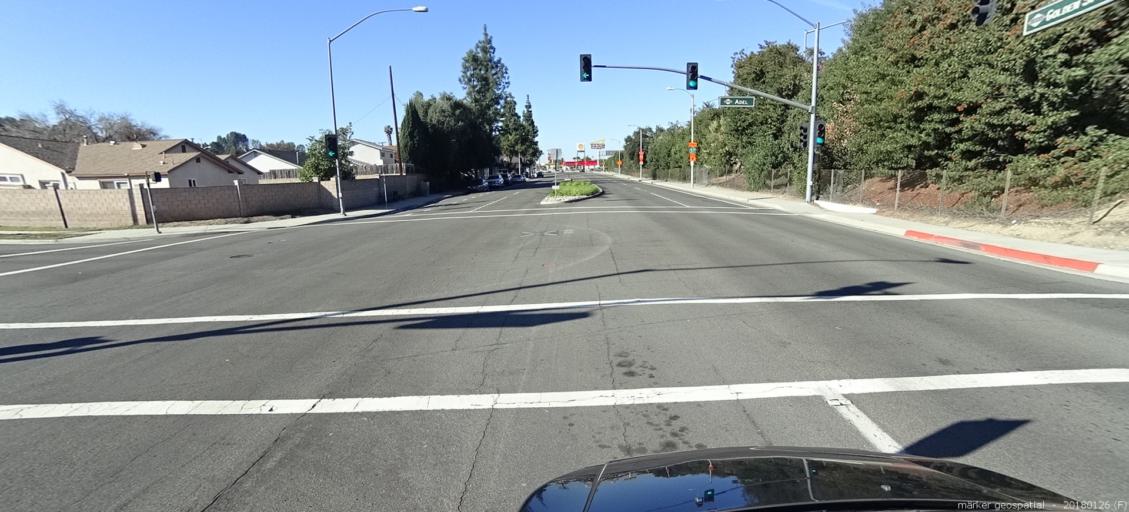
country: US
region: California
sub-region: Los Angeles County
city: Walnut
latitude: 34.0008
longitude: -117.8403
